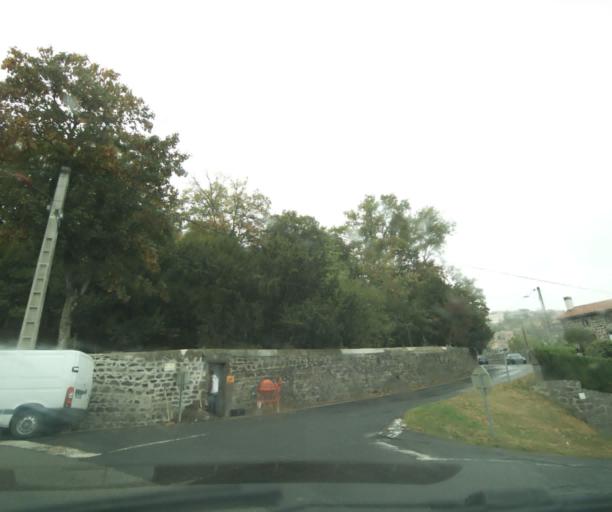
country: FR
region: Auvergne
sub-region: Departement du Puy-de-Dome
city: Chateaugay
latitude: 45.8497
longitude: 3.0892
